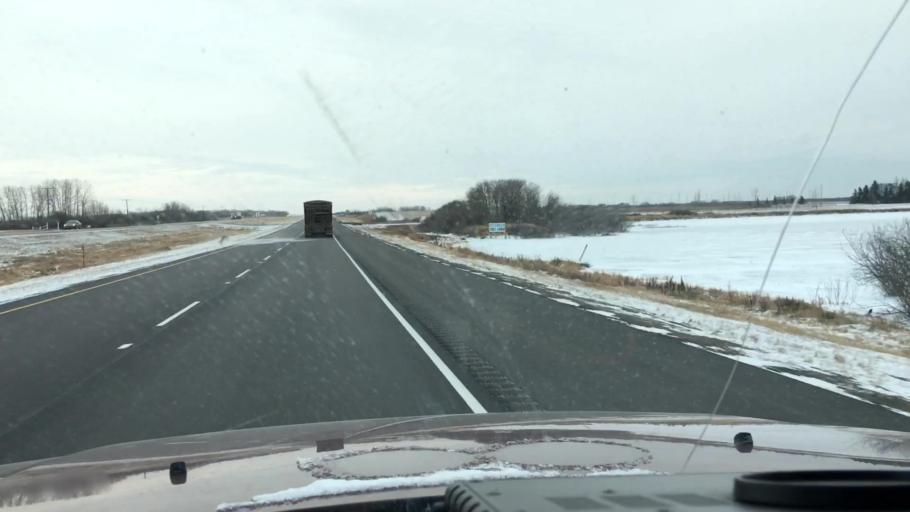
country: CA
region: Saskatchewan
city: Saskatoon
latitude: 51.9231
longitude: -106.5321
